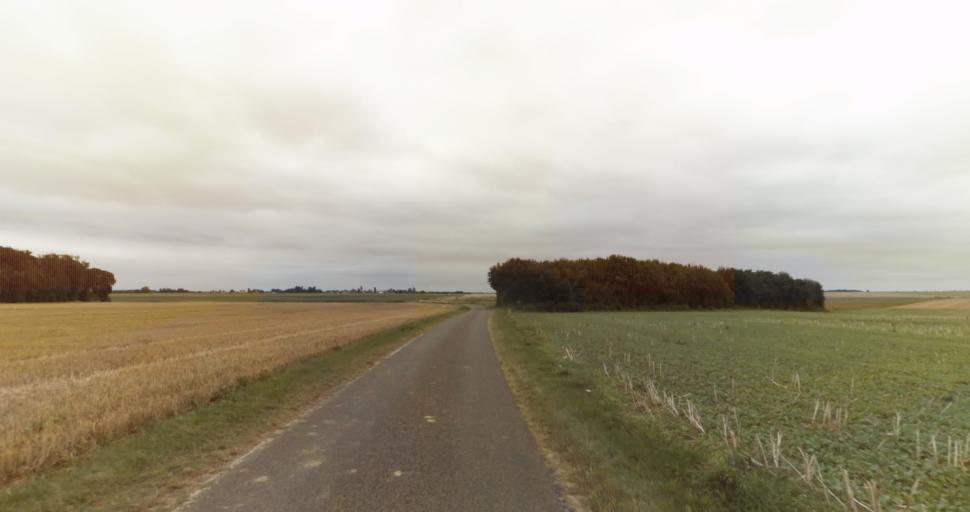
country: FR
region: Haute-Normandie
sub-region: Departement de l'Eure
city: La Couture-Boussey
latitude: 48.9186
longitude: 1.3569
